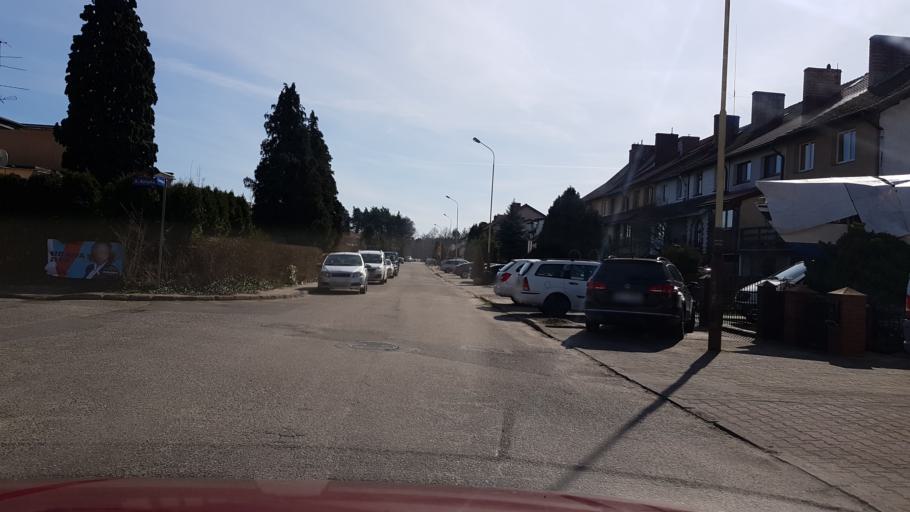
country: PL
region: West Pomeranian Voivodeship
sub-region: Powiat goleniowski
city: Goleniow
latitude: 53.5551
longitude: 14.8297
